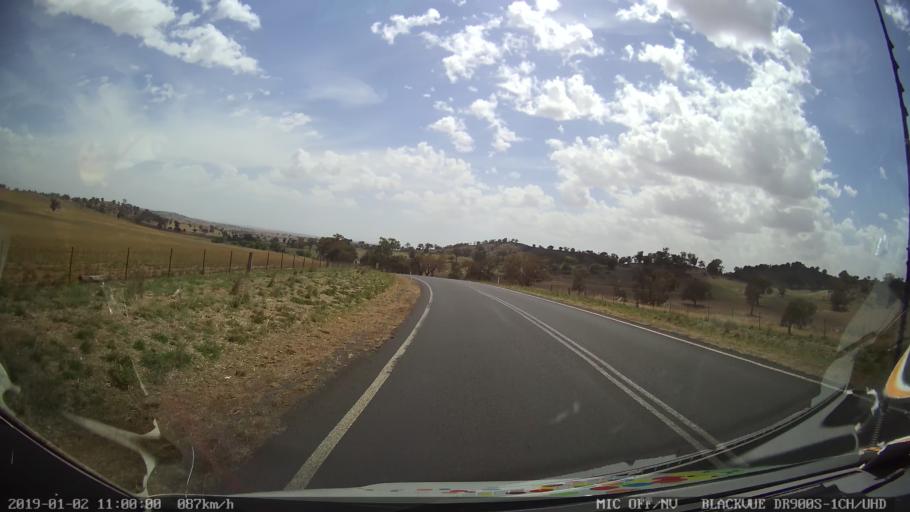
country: AU
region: New South Wales
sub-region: Cootamundra
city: Cootamundra
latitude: -34.6094
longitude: 148.3120
